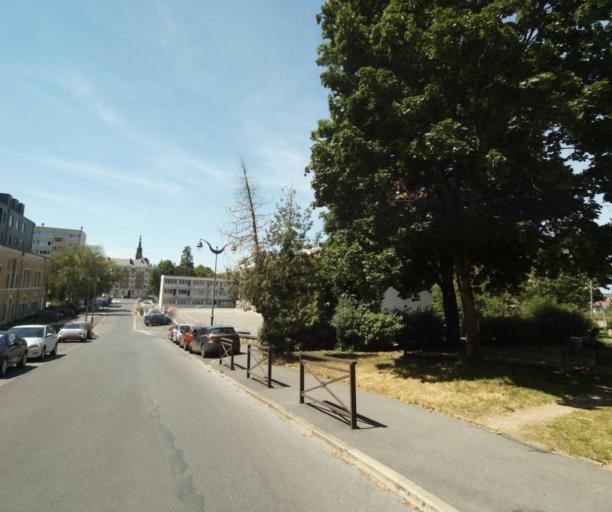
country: FR
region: Champagne-Ardenne
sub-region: Departement des Ardennes
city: Charleville-Mezieres
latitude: 49.7609
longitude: 4.7229
